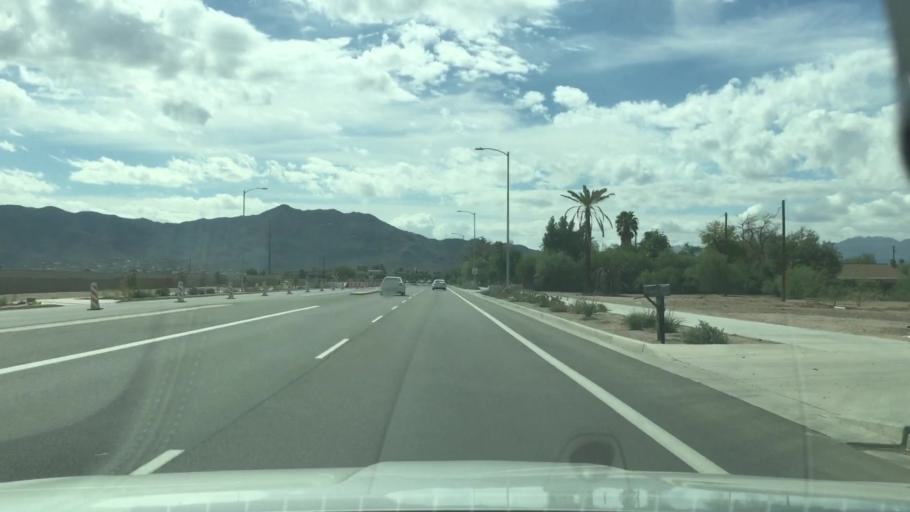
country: US
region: Arizona
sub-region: Maricopa County
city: Laveen
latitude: 33.3822
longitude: -112.1338
